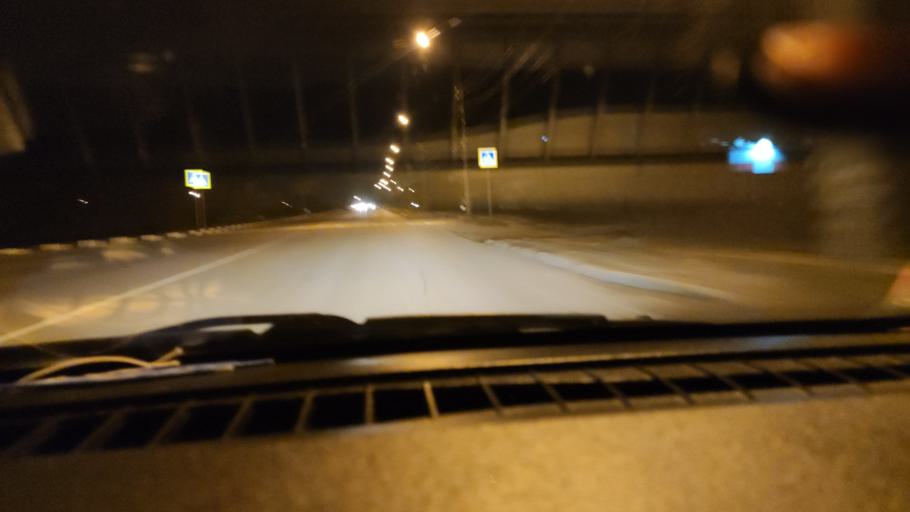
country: RU
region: Saratov
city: Privolzhskiy
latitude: 51.3938
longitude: 46.0343
